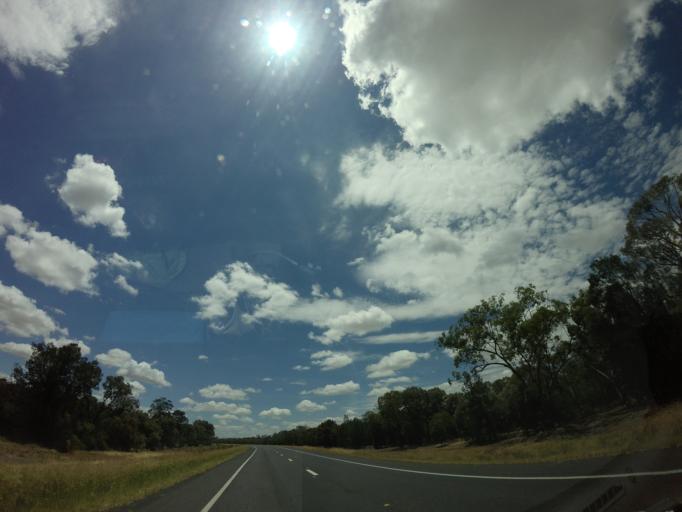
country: AU
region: New South Wales
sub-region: Moree Plains
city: Boggabilla
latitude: -28.8622
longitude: 150.2074
